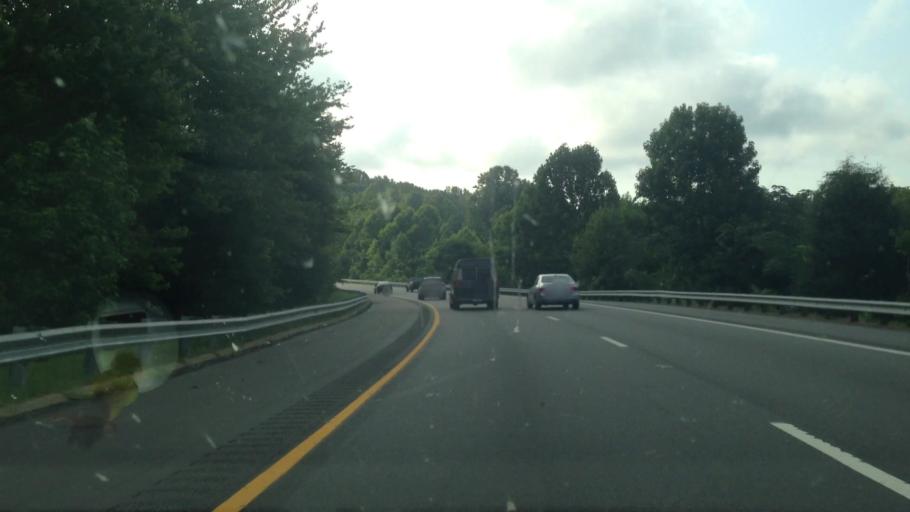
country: US
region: North Carolina
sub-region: Forsyth County
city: Kernersville
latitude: 36.0967
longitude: -80.0144
